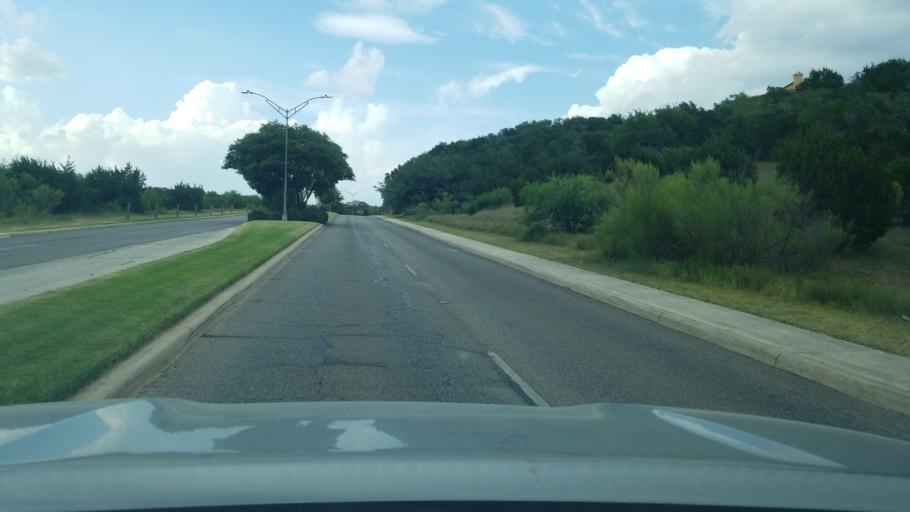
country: US
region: Texas
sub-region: Bexar County
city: Hollywood Park
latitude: 29.6480
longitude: -98.4811
